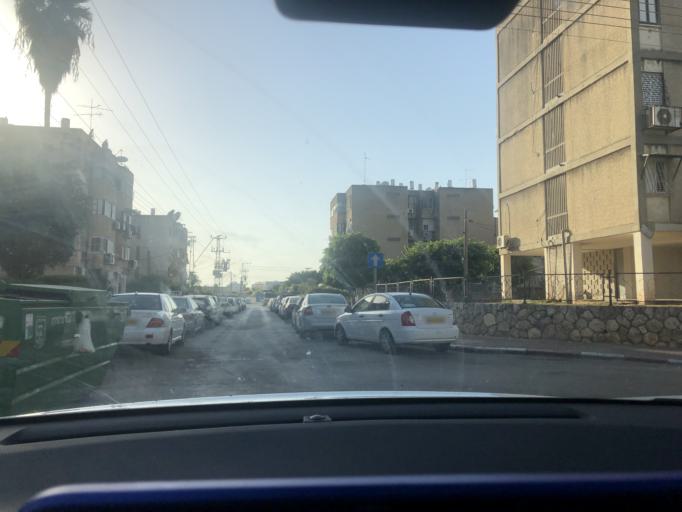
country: IL
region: Central District
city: Lod
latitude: 31.9513
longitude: 34.8880
